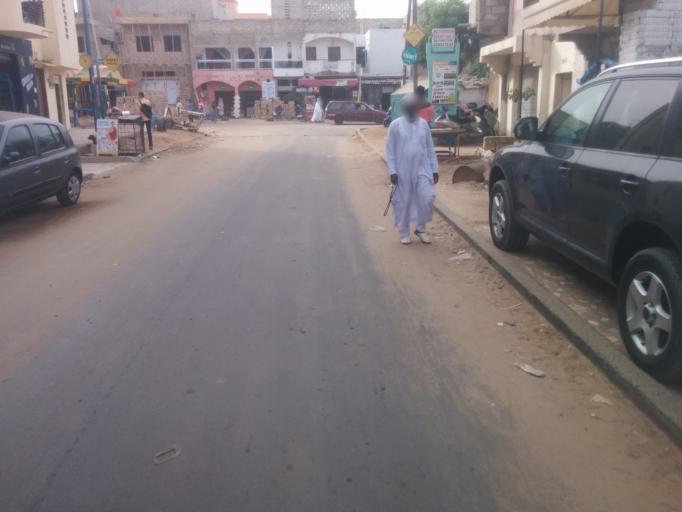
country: SN
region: Dakar
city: Grand Dakar
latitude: 14.7530
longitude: -17.4428
